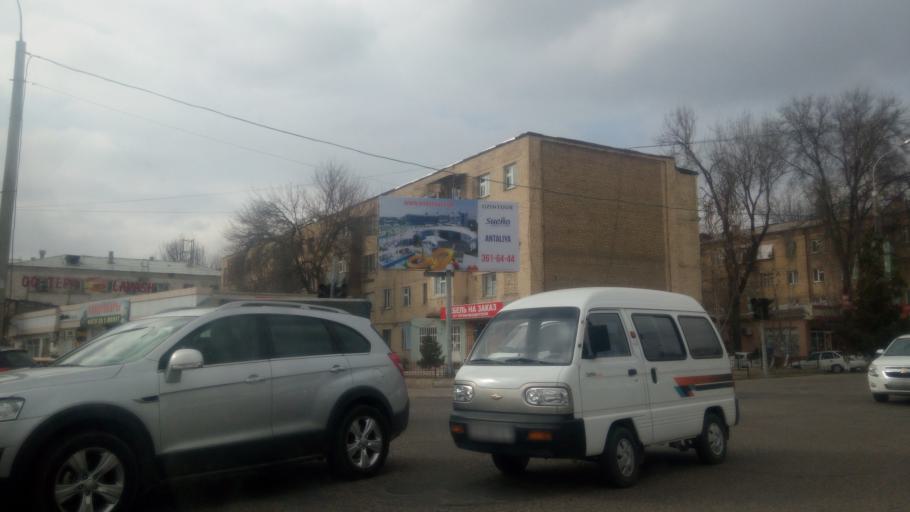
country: UZ
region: Toshkent Shahri
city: Tashkent
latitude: 41.3483
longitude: 69.2523
